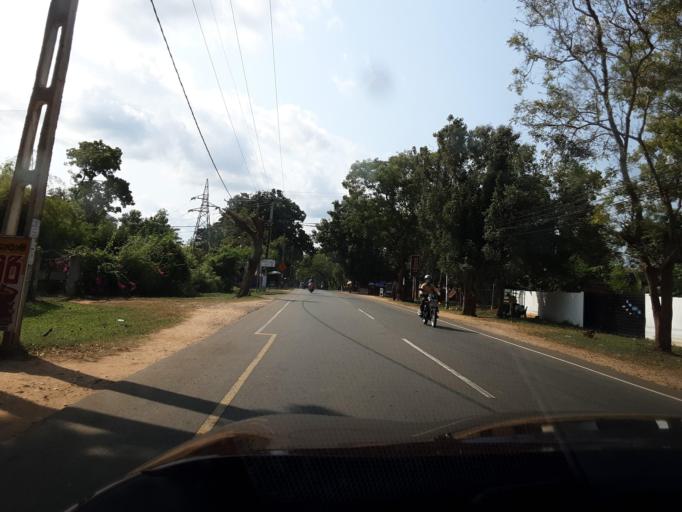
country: LK
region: Uva
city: Haputale
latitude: 6.3504
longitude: 81.1952
